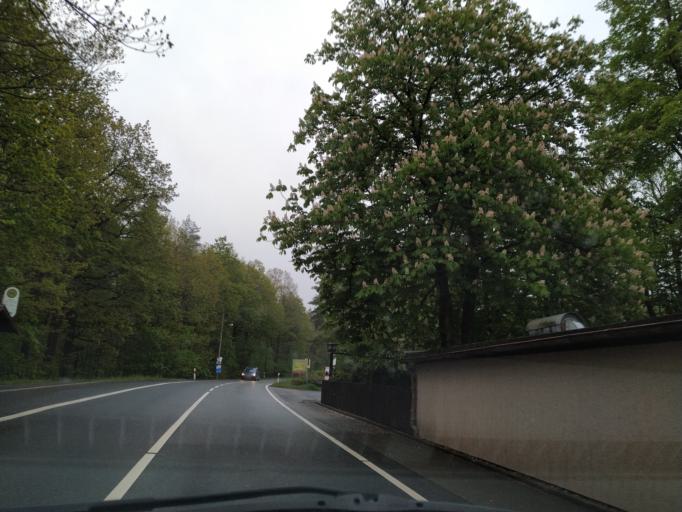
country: DE
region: Saxony
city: Hartmannsdorf
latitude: 50.7771
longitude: 12.4279
